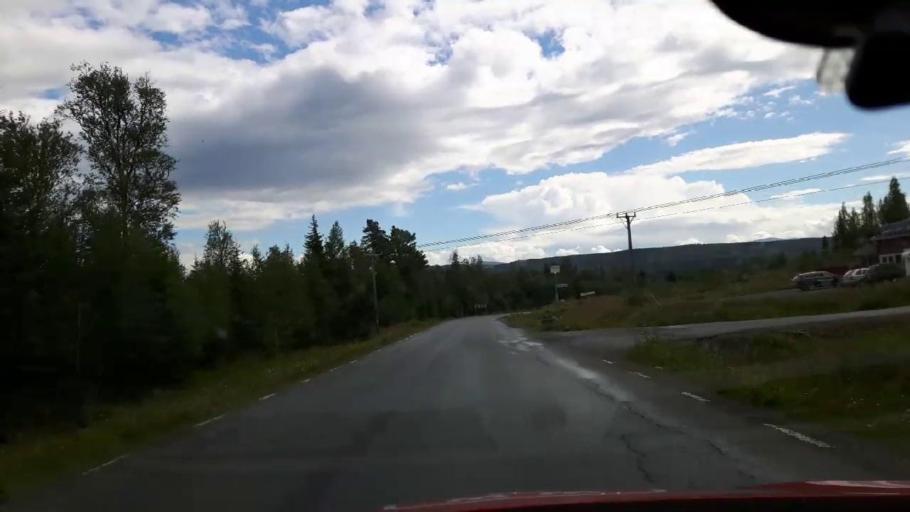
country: SE
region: Jaemtland
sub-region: Are Kommun
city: Are
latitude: 63.3216
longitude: 13.2330
